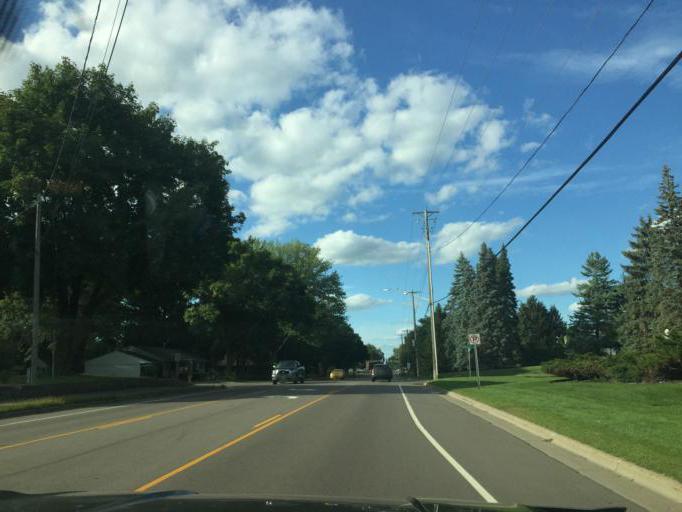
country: US
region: Minnesota
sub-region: Ramsey County
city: Roseville
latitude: 44.9960
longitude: -93.1463
